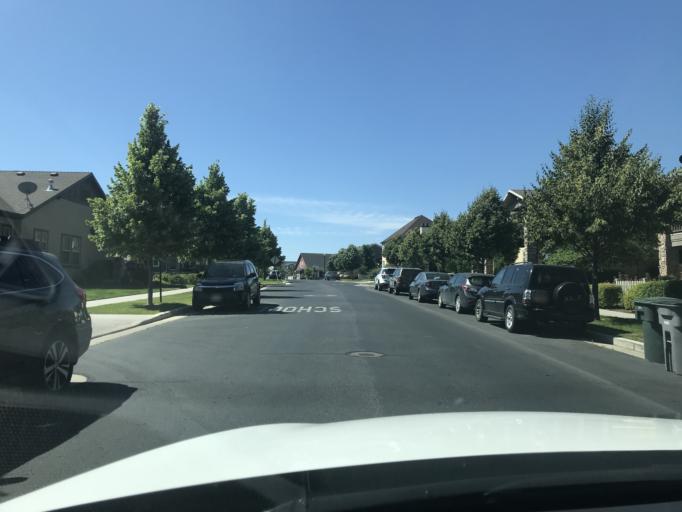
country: US
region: Utah
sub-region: Salt Lake County
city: South Jordan Heights
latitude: 40.5569
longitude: -111.9975
